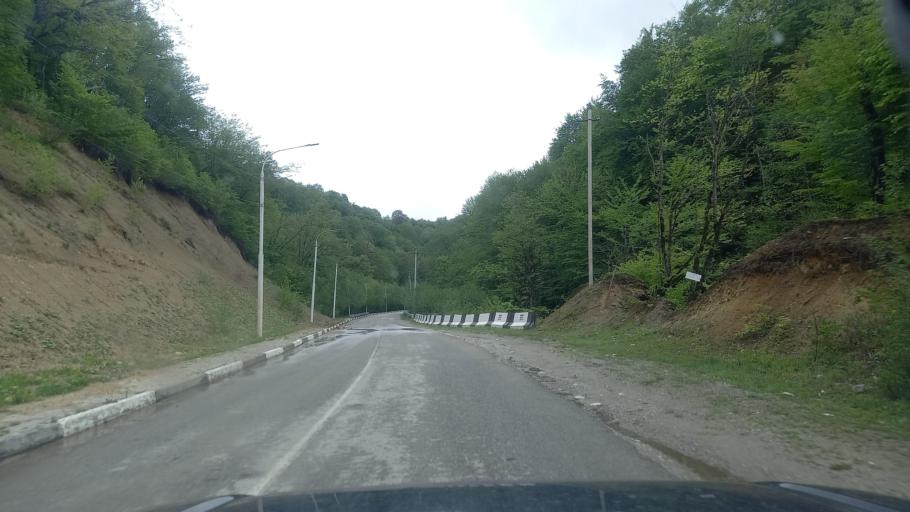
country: RU
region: Kabardino-Balkariya
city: Babugent
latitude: 43.2360
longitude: 43.5410
